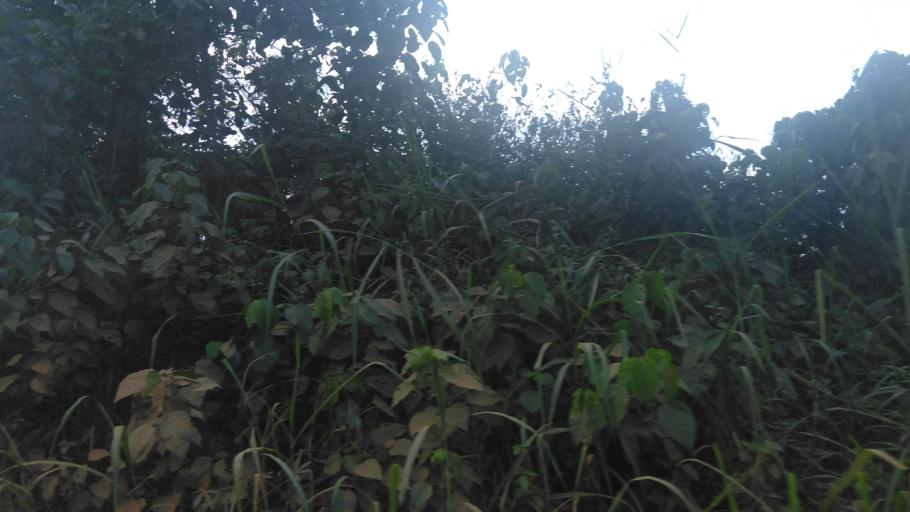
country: NG
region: Osun
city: Ifetedo
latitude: 7.0118
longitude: 4.6354
